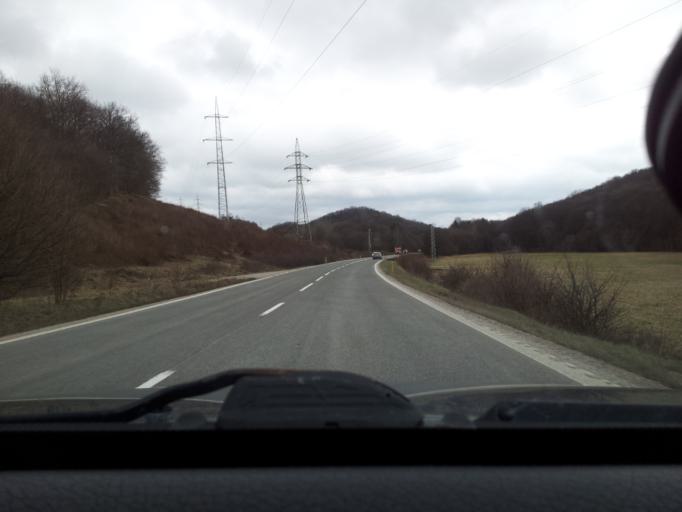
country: SK
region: Kosicky
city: Roznava
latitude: 48.6138
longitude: 20.6339
